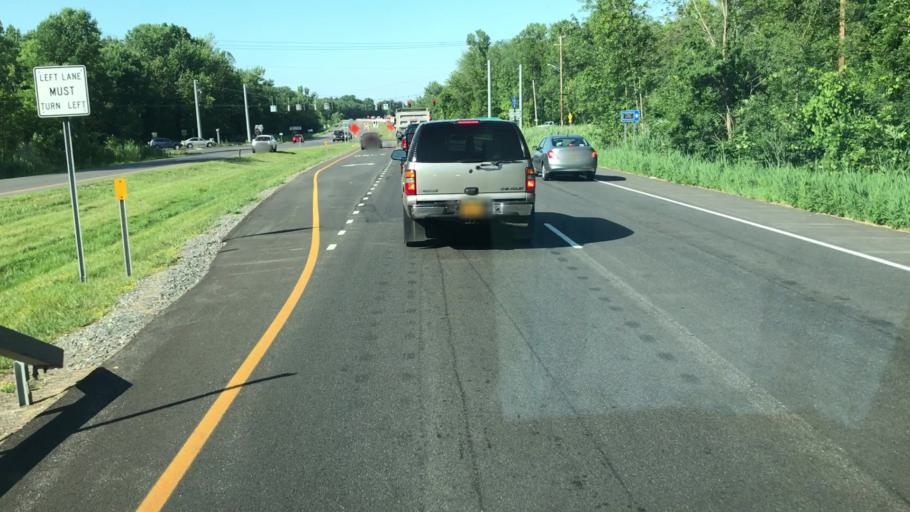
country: US
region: New York
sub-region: Onondaga County
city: Liverpool
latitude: 43.1259
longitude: -76.2448
